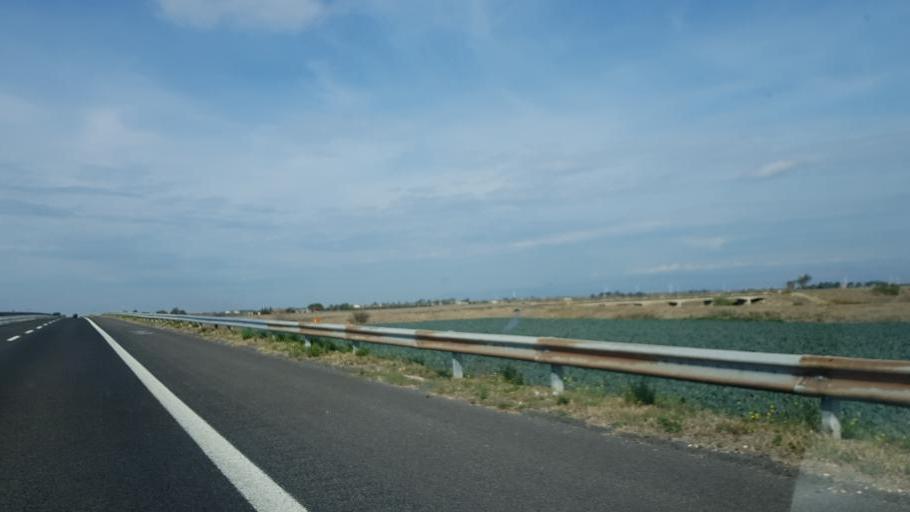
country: IT
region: Apulia
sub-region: Provincia di Foggia
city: Carapelle
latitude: 41.3777
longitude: 15.7586
